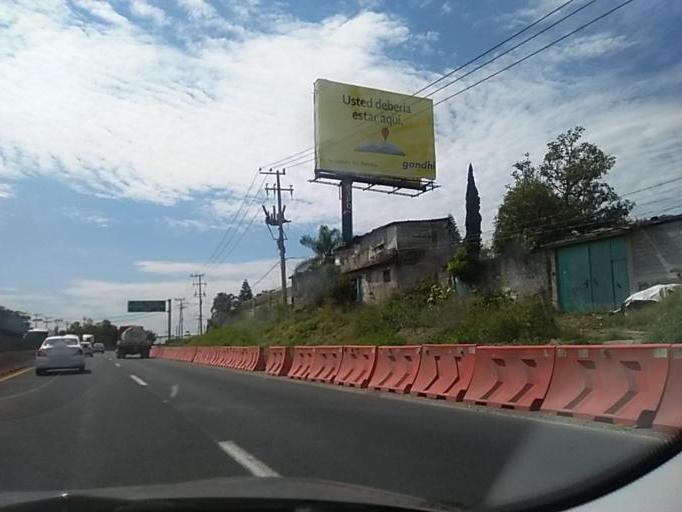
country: MX
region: Morelos
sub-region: Cuernavaca
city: Colonia los Cerritos
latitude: 18.9416
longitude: -99.1900
